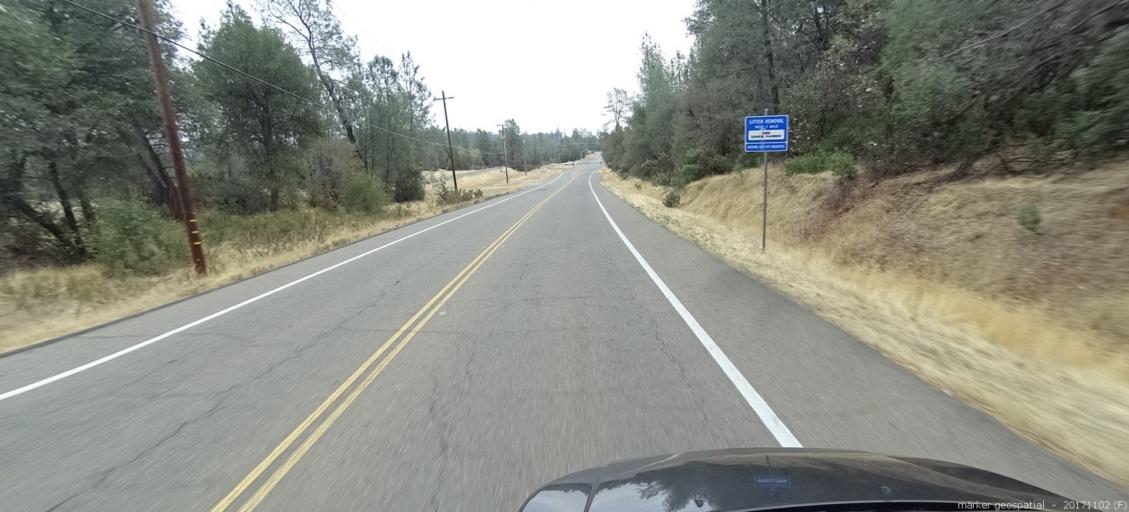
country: US
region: California
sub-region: Shasta County
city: Central Valley (historical)
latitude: 40.6636
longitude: -122.3918
